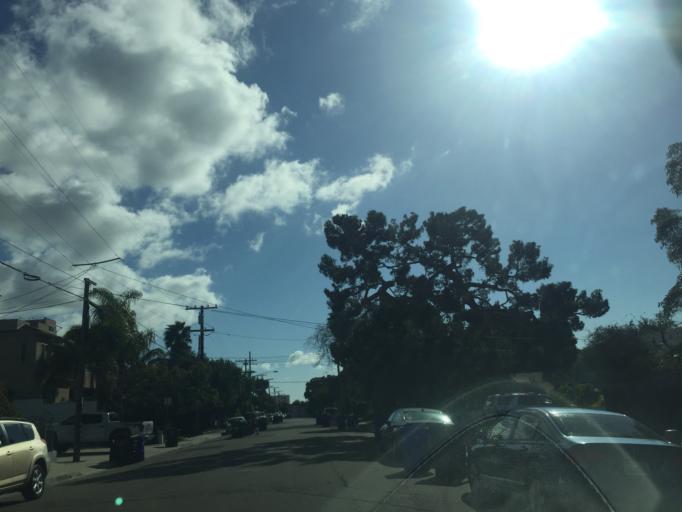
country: US
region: California
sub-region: San Diego County
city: La Jolla
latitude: 32.7933
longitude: -117.2428
